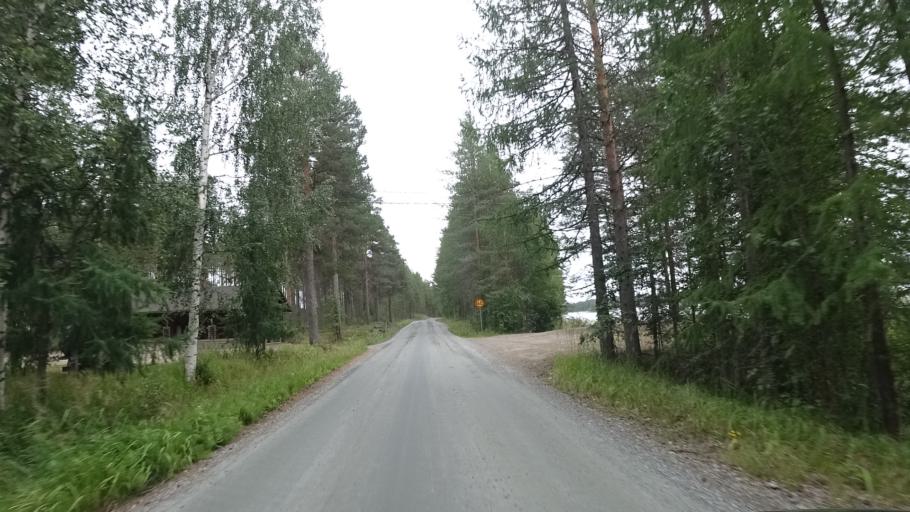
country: FI
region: North Karelia
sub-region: Pielisen Karjala
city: Lieksa
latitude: 63.3853
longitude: 30.3383
